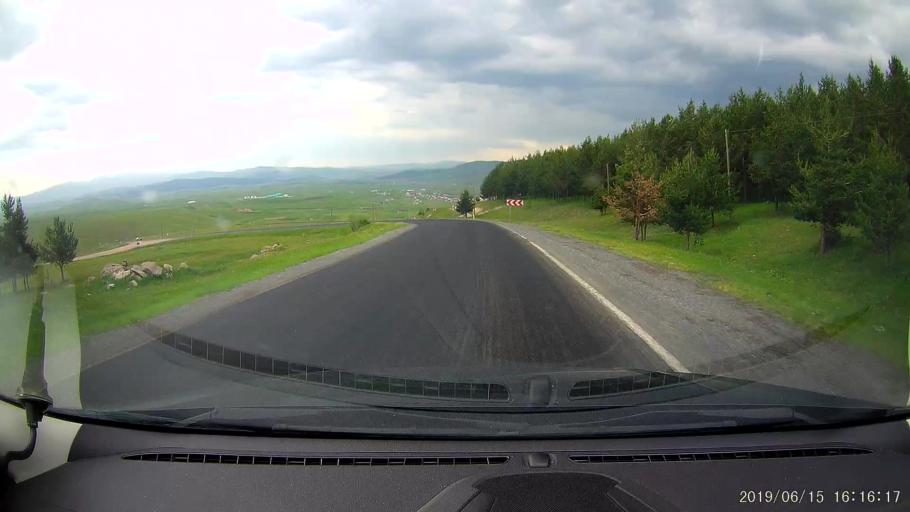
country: TR
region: Ardahan
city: Hanak
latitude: 41.2602
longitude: 42.8525
